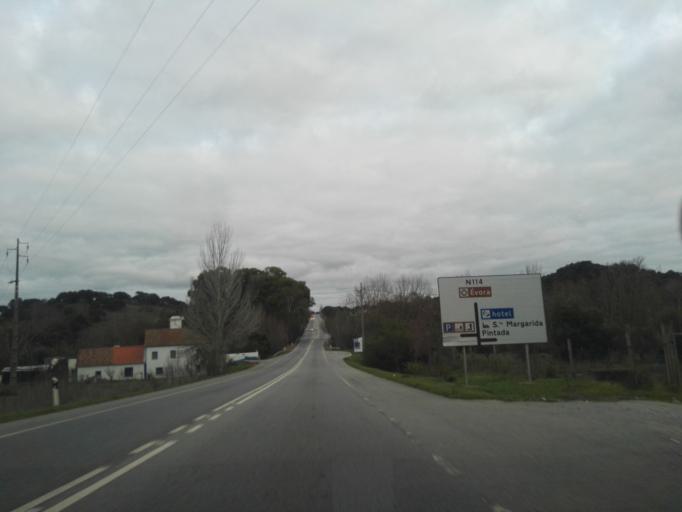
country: PT
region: Evora
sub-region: Montemor-O-Novo
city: Montemor-o-Novo
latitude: 38.6448
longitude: -8.1938
